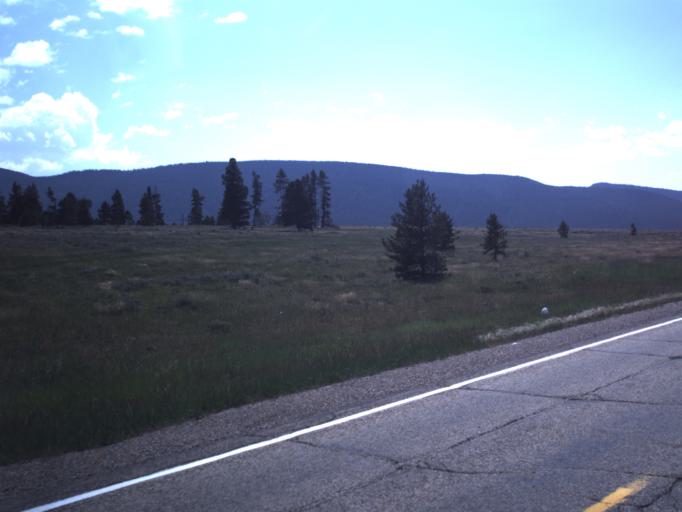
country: US
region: Utah
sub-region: Daggett County
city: Manila
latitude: 40.8001
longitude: -109.4665
